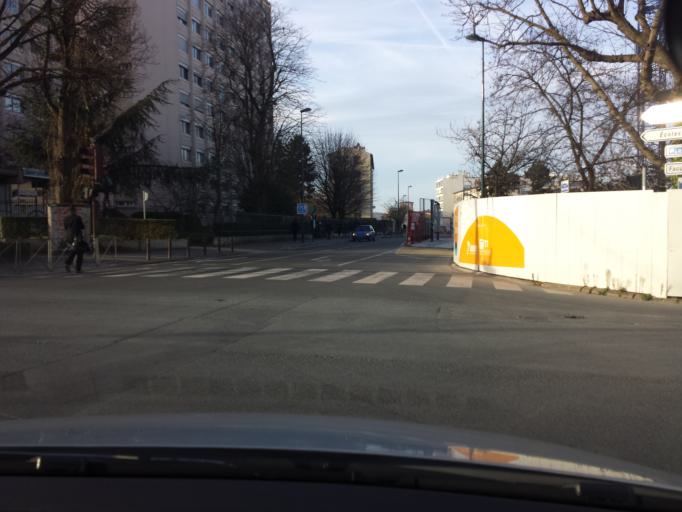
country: FR
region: Ile-de-France
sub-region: Departement de l'Essonne
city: Palaiseau
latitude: 48.7226
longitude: 2.2624
